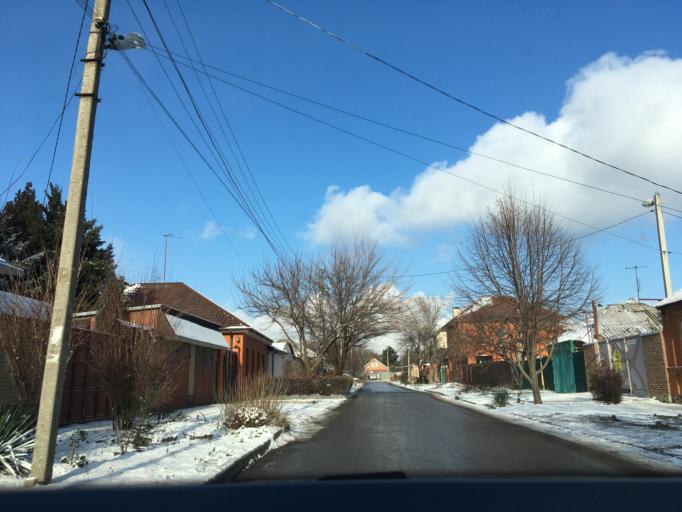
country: RU
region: Rostov
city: Rostov-na-Donu
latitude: 47.2346
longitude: 39.6294
